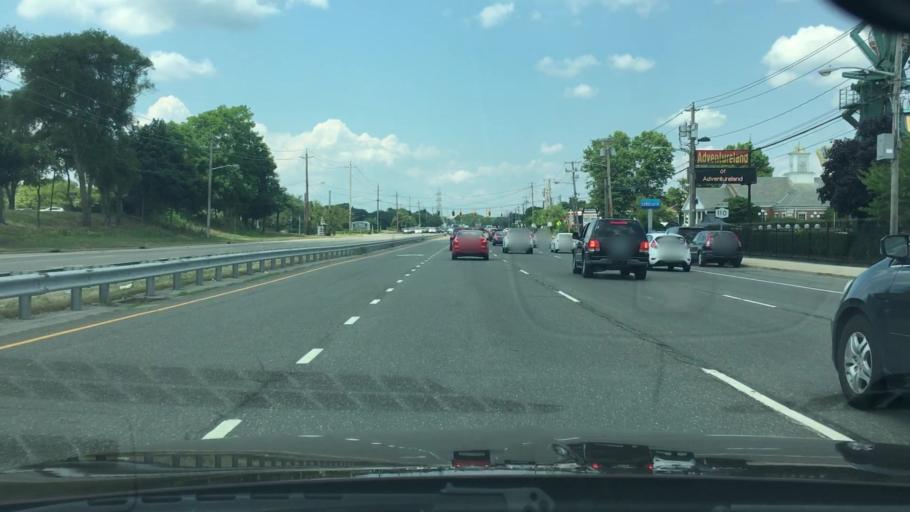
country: US
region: New York
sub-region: Suffolk County
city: East Farmingdale
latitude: 40.7521
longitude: -73.4221
